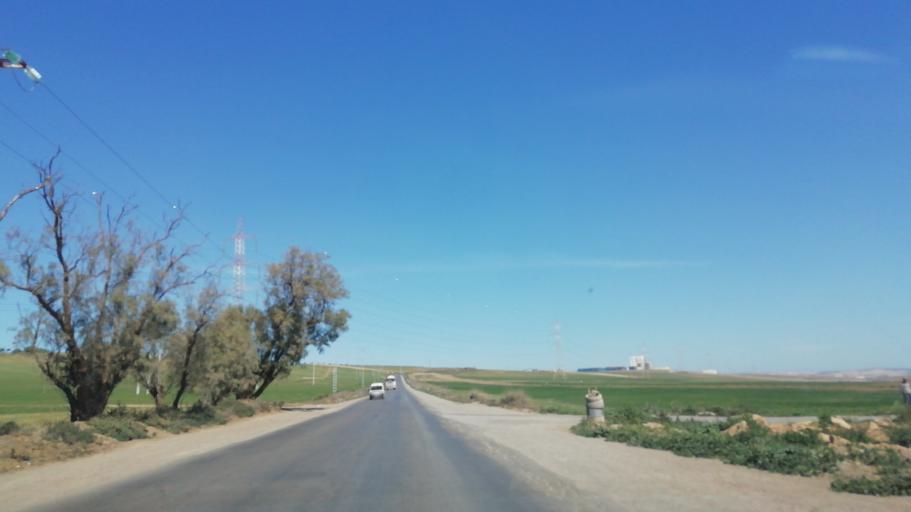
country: DZ
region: Oran
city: Es Senia
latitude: 35.5343
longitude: -0.5853
